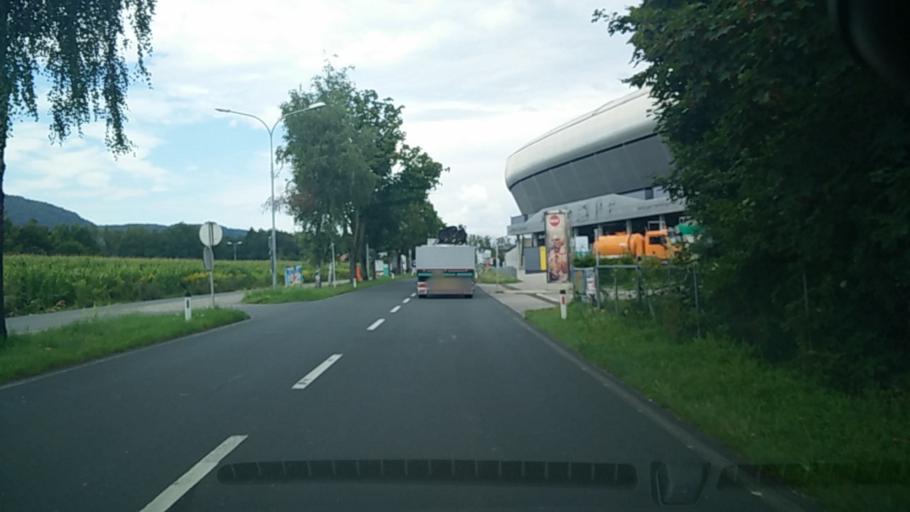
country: AT
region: Carinthia
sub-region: Klagenfurt am Woerthersee
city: Klagenfurt am Woerthersee
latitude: 46.6075
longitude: 14.2800
